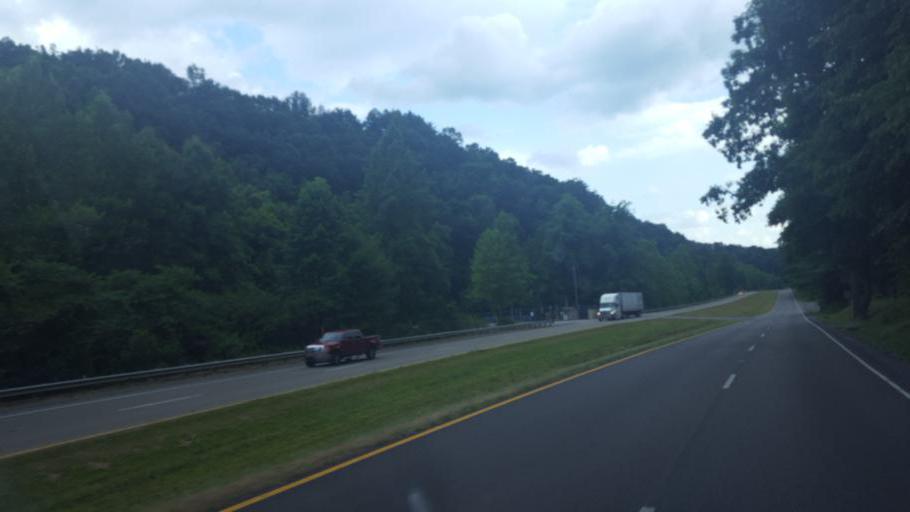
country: US
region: Virginia
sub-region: Wise County
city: Pound
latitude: 37.0814
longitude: -82.5986
